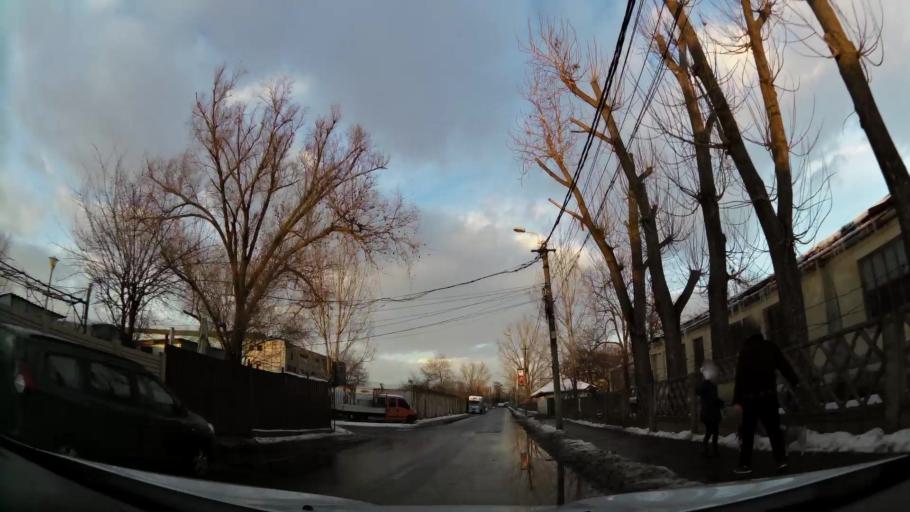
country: RO
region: Ilfov
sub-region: Comuna Popesti-Leordeni
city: Popesti-Leordeni
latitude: 44.3819
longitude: 26.1435
